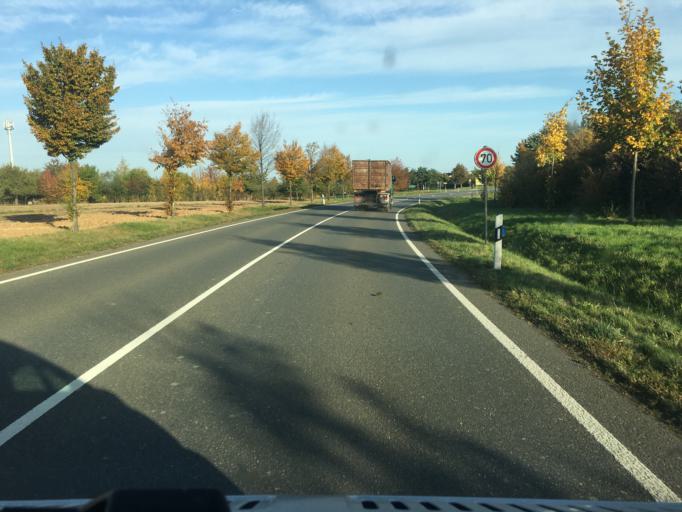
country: DE
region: Thuringia
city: Heyersdorf
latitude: 50.8434
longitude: 12.3350
